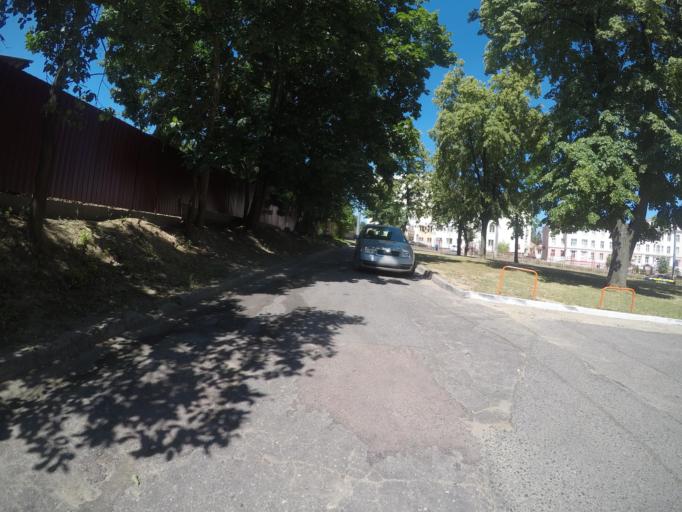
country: BY
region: Grodnenskaya
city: Hrodna
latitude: 53.6902
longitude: 23.8329
